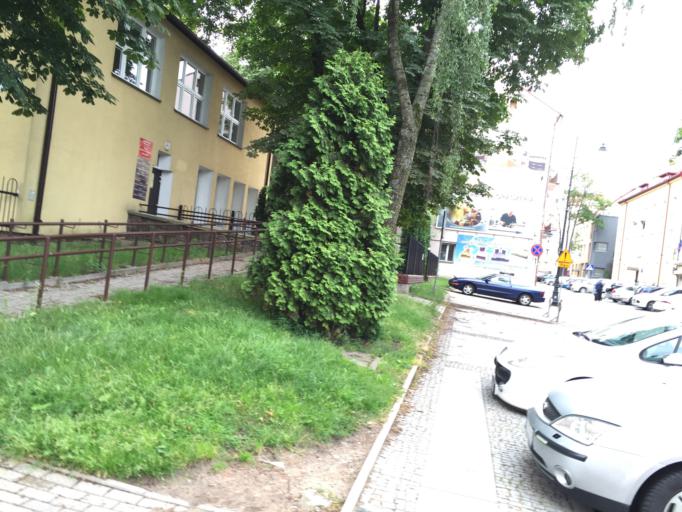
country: PL
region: Podlasie
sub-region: Bialystok
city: Bialystok
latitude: 53.1347
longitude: 23.1610
